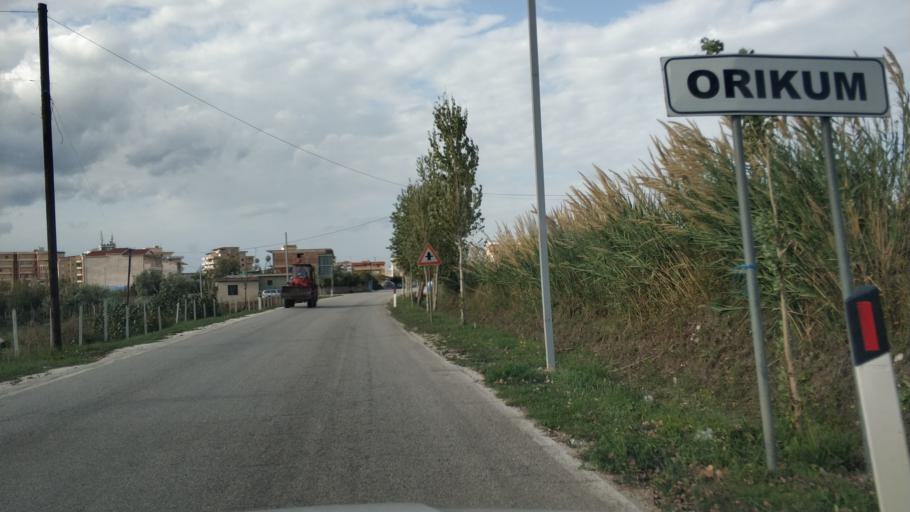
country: AL
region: Vlore
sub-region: Rrethi i Vlores
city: Orikum
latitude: 40.3257
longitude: 19.4792
